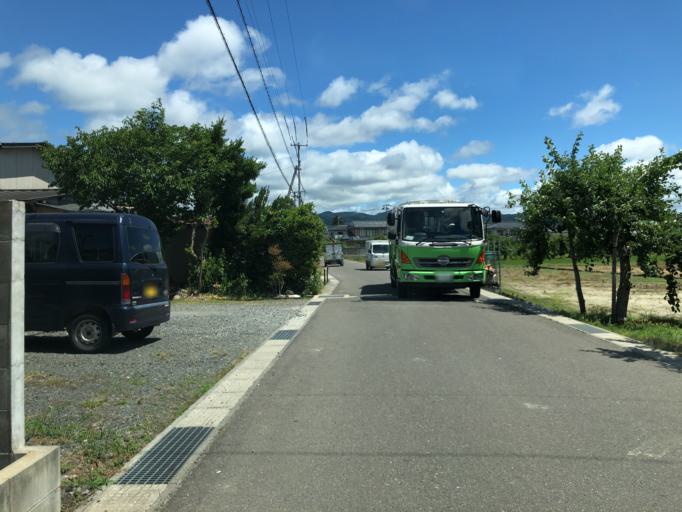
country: JP
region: Fukushima
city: Fukushima-shi
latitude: 37.8032
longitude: 140.4359
